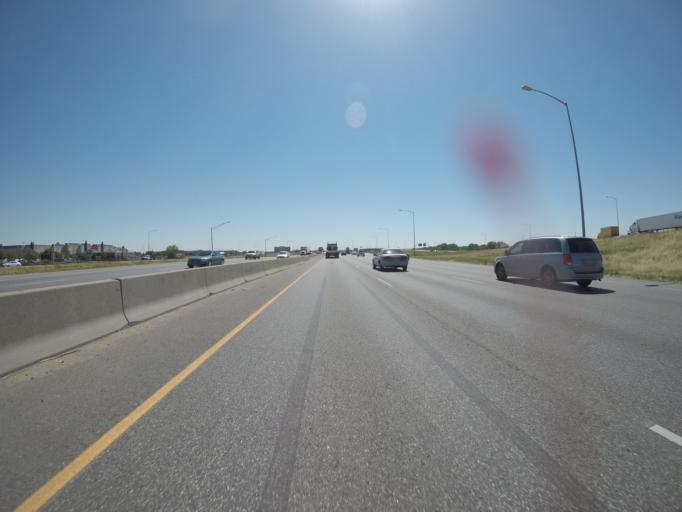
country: US
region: Colorado
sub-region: Adams County
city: Commerce City
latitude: 39.7782
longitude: -104.8951
